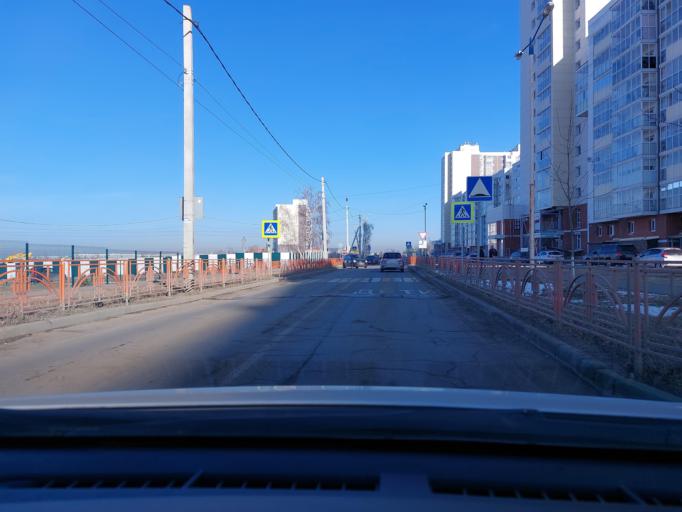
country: RU
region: Irkutsk
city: Smolenshchina
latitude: 52.3510
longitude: 104.1435
